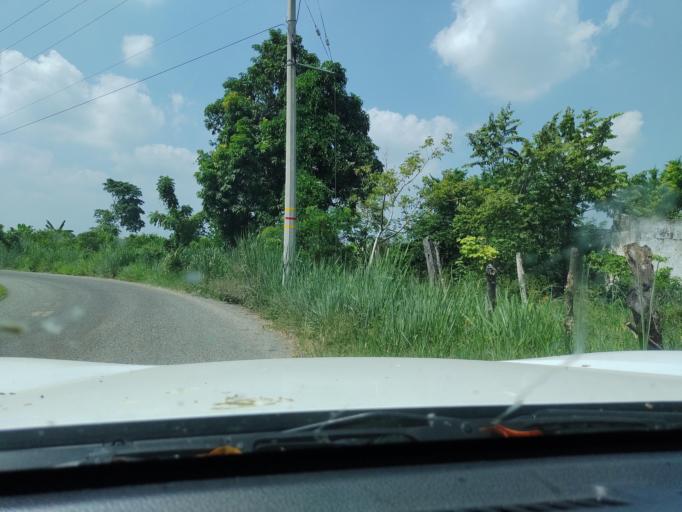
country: MX
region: Veracruz
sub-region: Atzalan
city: Colonias Pedernales
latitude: 20.0639
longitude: -97.0251
